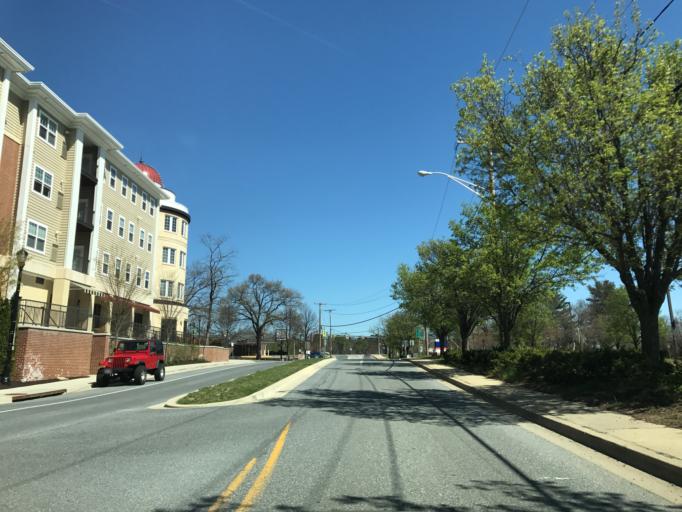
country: US
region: Maryland
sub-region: Anne Arundel County
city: Odenton
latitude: 39.0883
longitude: -76.7080
